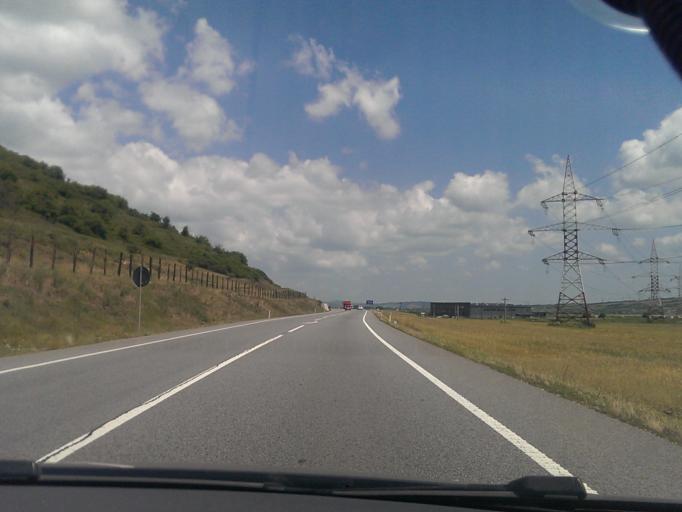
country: RO
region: Cluj
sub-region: Comuna Apahida
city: Apahida
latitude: 46.8161
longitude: 23.7389
